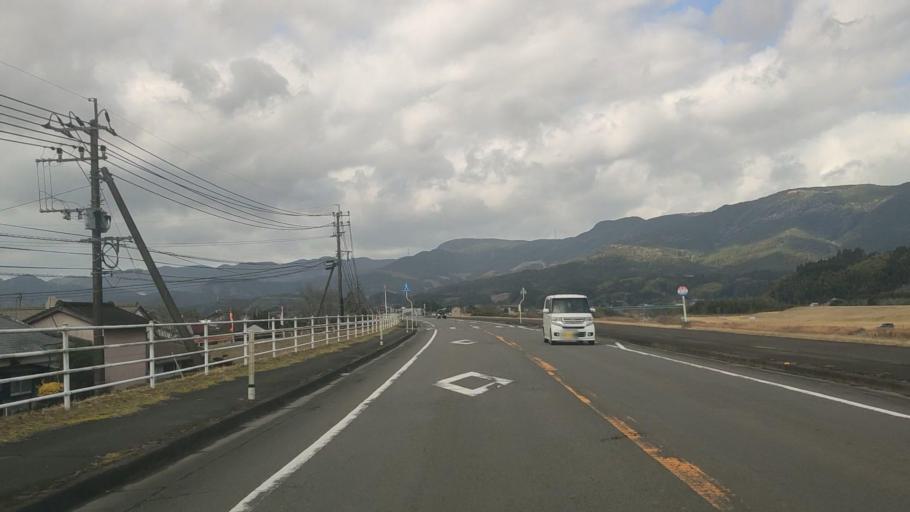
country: JP
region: Kumamoto
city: Hitoyoshi
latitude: 32.0550
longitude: 130.7974
